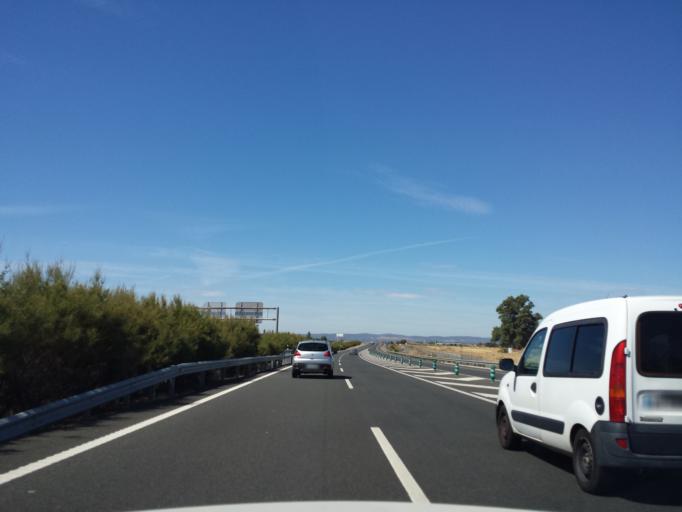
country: ES
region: Extremadura
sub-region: Provincia de Caceres
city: Millanes
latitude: 39.8659
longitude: -5.5992
